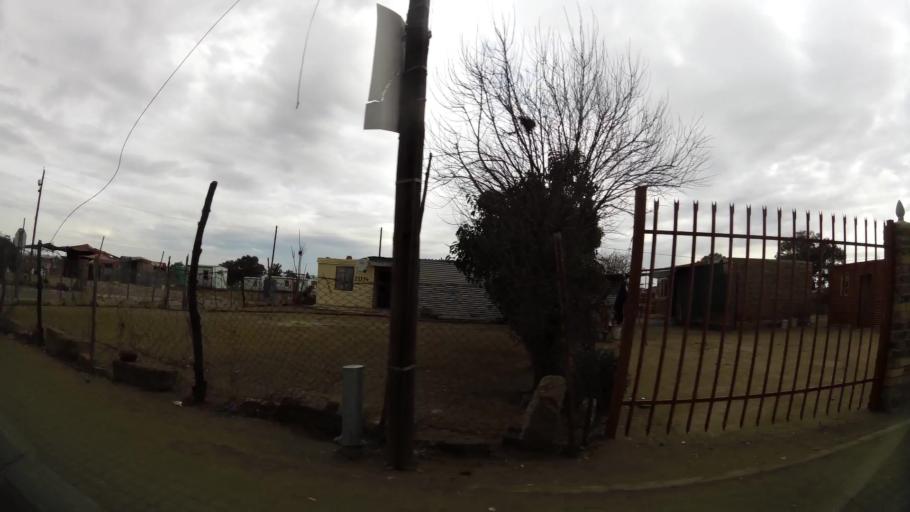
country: ZA
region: Orange Free State
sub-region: Fezile Dabi District Municipality
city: Kroonstad
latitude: -27.6504
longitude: 27.2213
